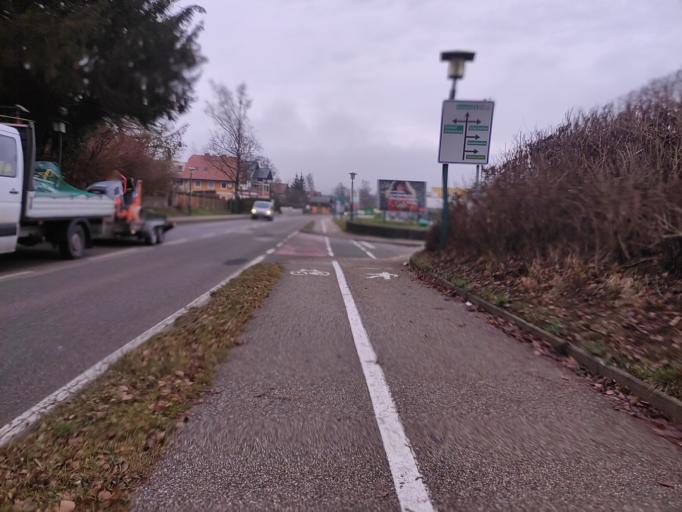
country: AT
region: Salzburg
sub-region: Politischer Bezirk Salzburg-Umgebung
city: Neumarkt am Wallersee
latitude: 47.9395
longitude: 13.2237
